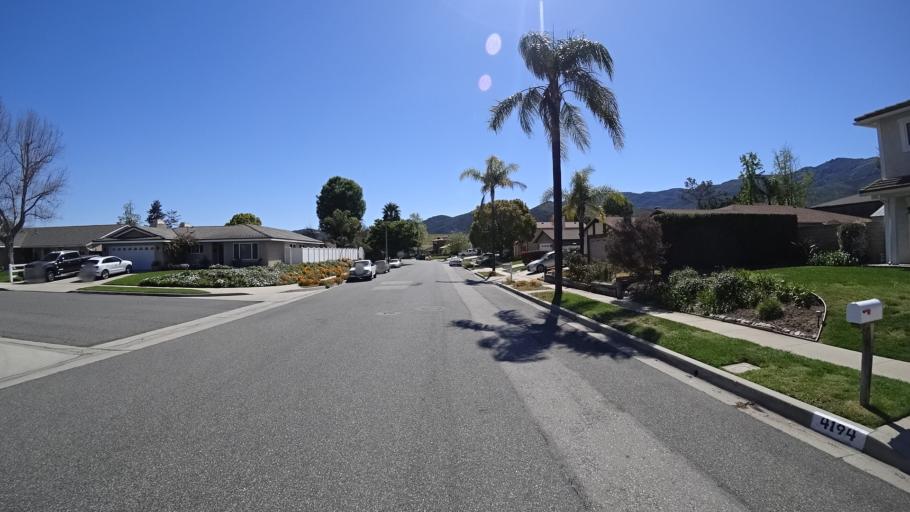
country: US
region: California
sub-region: Ventura County
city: Casa Conejo
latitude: 34.1575
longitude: -118.9638
